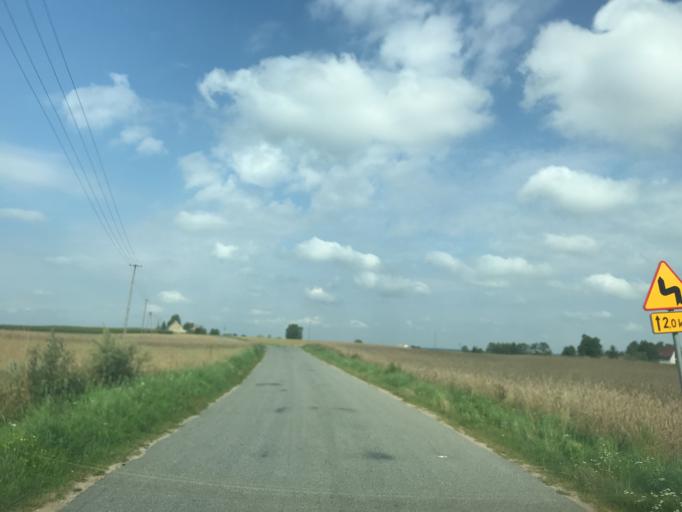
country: PL
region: Warmian-Masurian Voivodeship
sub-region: Powiat nowomiejski
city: Kurzetnik
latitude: 53.3983
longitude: 19.4717
